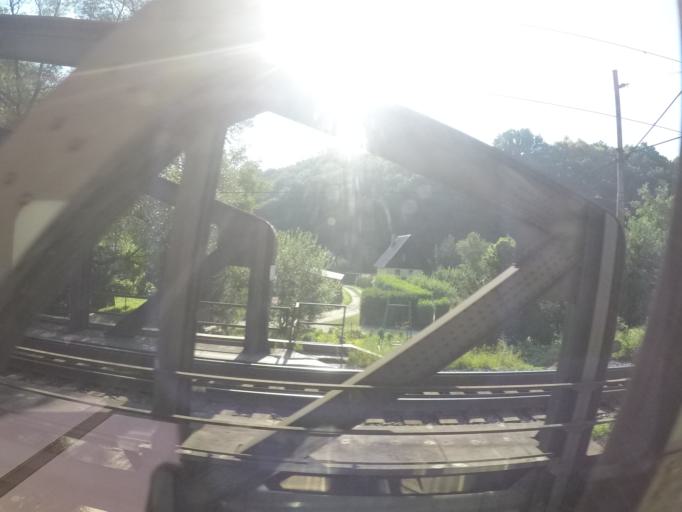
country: SK
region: Kosicky
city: Kosice
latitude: 48.7820
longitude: 21.2440
